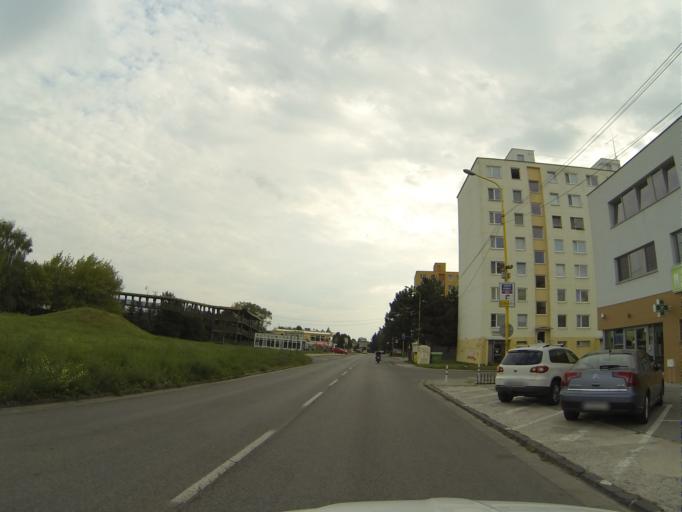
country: SK
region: Nitriansky
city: Prievidza
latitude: 48.7796
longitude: 18.6197
